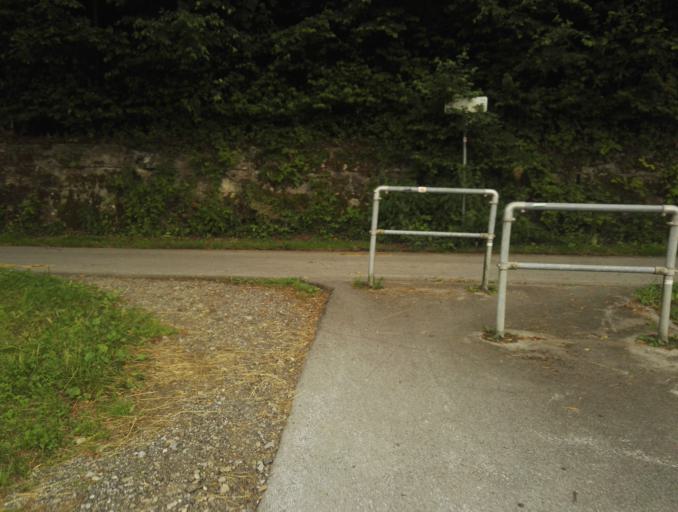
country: AT
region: Styria
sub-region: Politischer Bezirk Graz-Umgebung
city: Gratkorn
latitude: 47.1179
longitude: 15.3558
